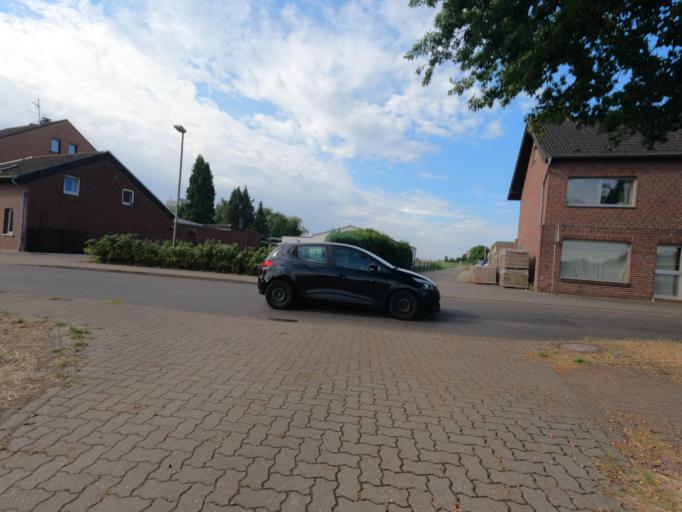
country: DE
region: North Rhine-Westphalia
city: Wegberg
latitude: 51.1116
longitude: 6.2586
